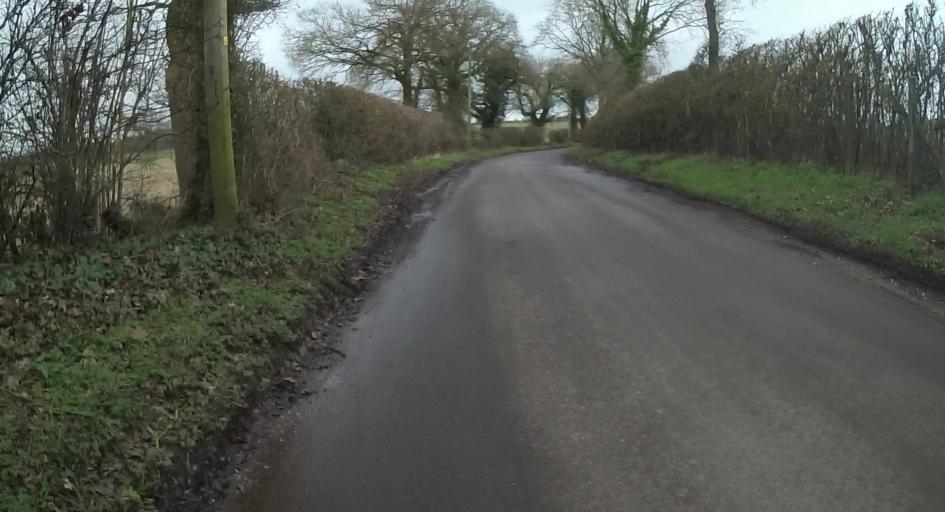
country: GB
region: England
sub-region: Hampshire
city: Overton
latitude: 51.2625
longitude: -1.1960
